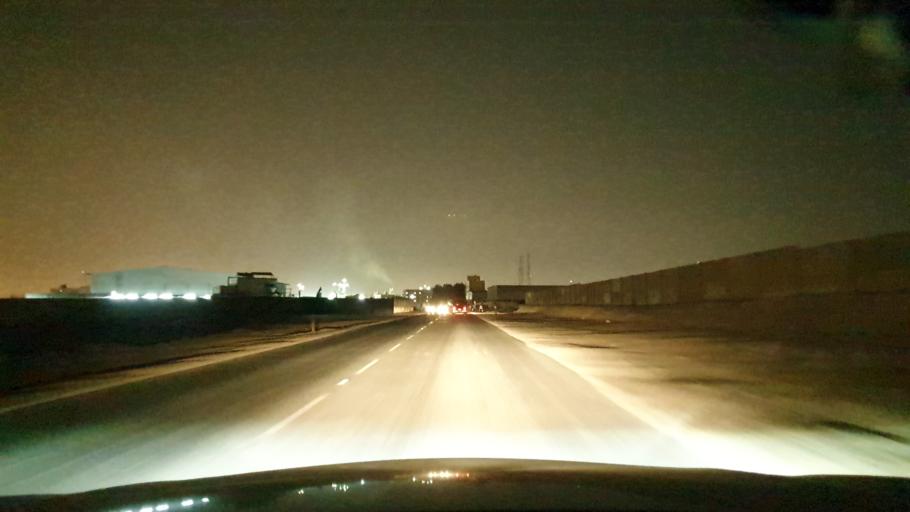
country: BH
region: Northern
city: Sitrah
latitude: 26.0896
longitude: 50.6162
